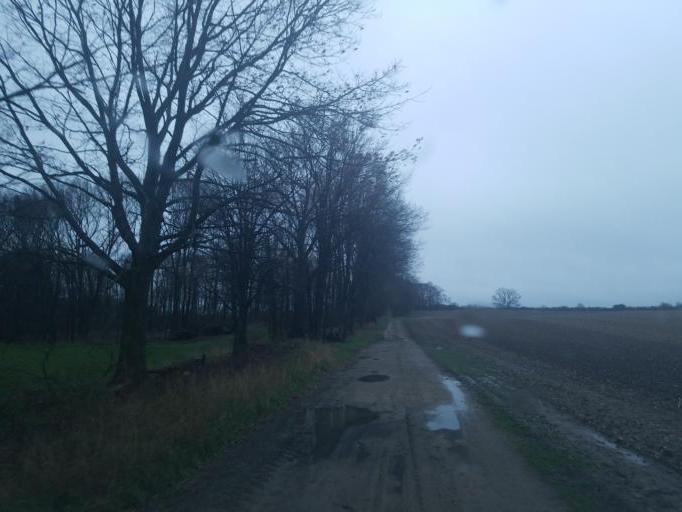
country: US
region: Michigan
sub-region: Montcalm County
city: Edmore
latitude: 43.4709
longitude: -85.0250
